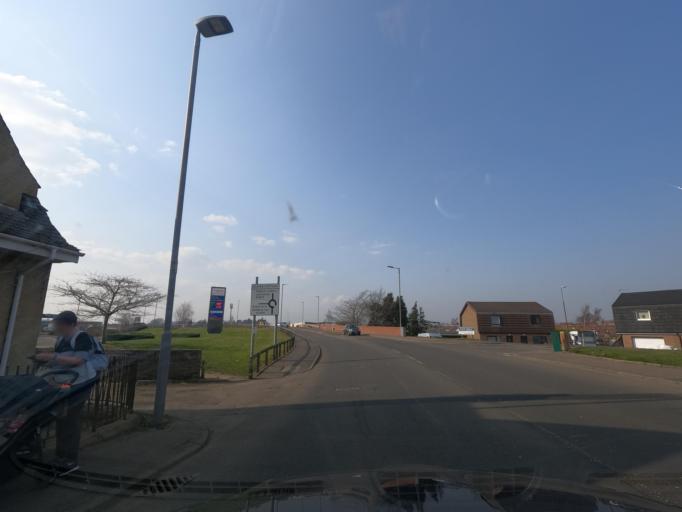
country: GB
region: Scotland
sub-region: Falkirk
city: Polmont
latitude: 55.9850
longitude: -3.7317
